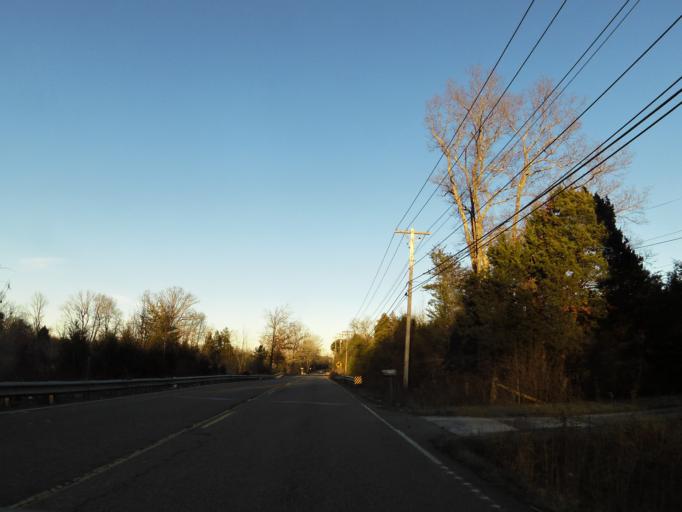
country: US
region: Tennessee
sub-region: Knox County
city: Mascot
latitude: 36.0134
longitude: -83.7621
